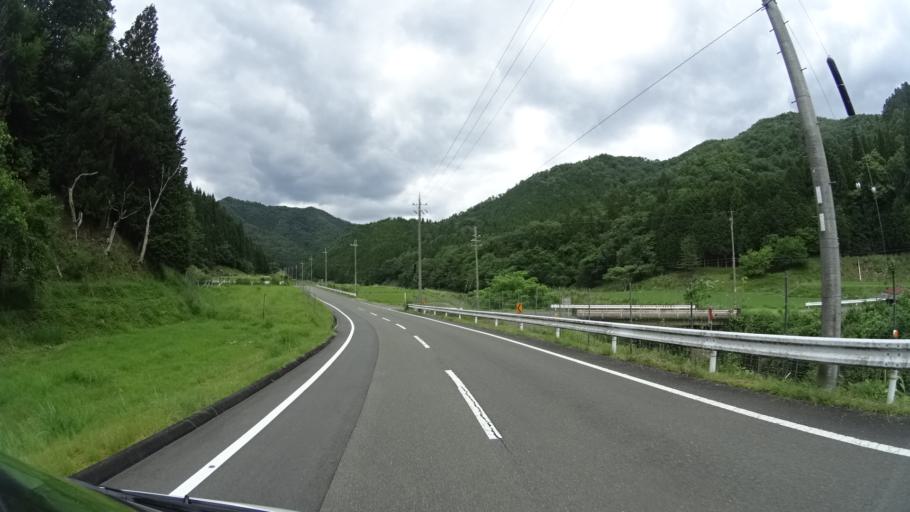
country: JP
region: Hyogo
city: Sasayama
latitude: 35.0531
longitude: 135.4021
